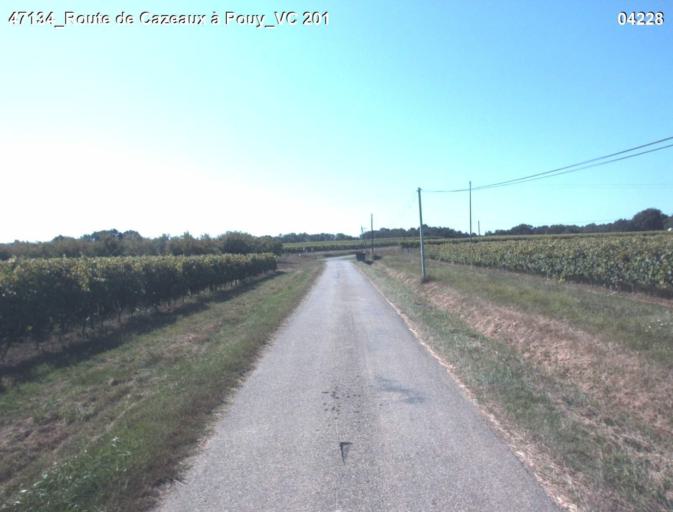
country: FR
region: Aquitaine
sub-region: Departement du Lot-et-Garonne
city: Mezin
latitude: 44.0344
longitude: 0.3116
